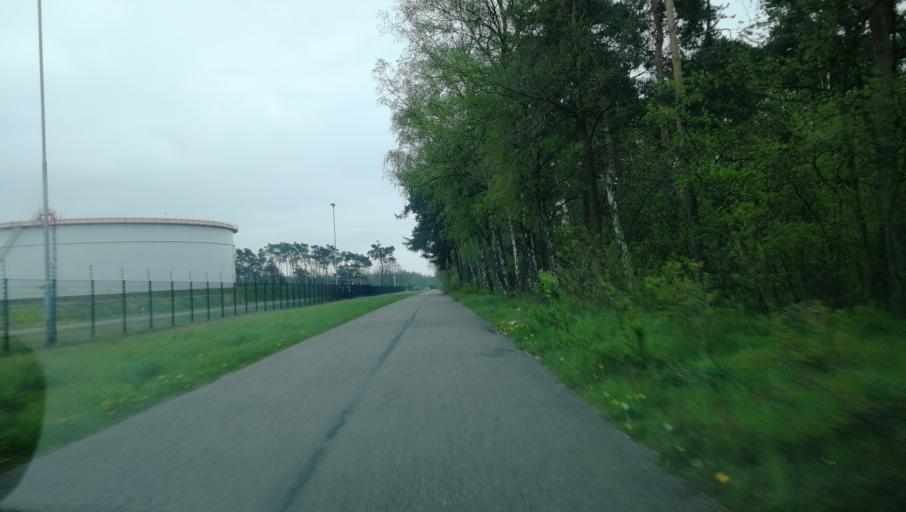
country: NL
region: Limburg
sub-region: Gemeente Venlo
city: Venlo
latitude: 51.3774
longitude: 6.2155
